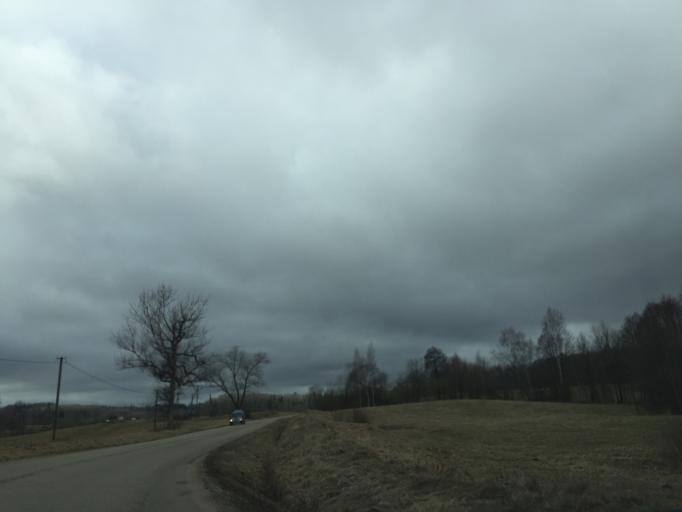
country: LV
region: Ilukste
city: Ilukste
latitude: 56.0170
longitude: 26.2499
